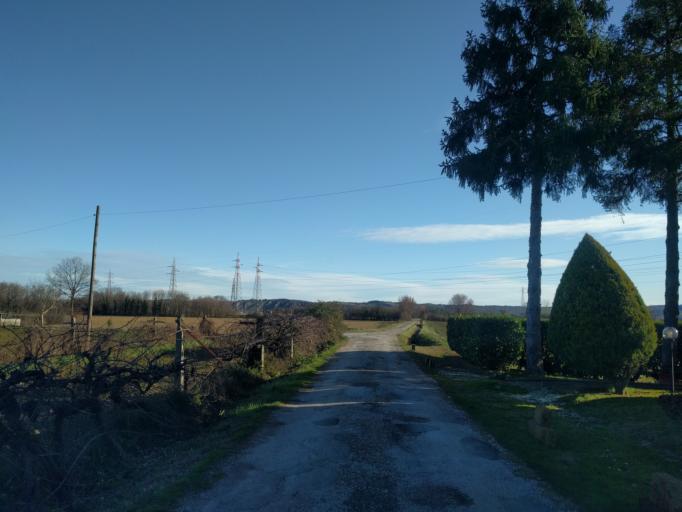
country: IT
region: The Marches
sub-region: Provincia di Pesaro e Urbino
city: Cuccurano
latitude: 43.7863
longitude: 12.9486
